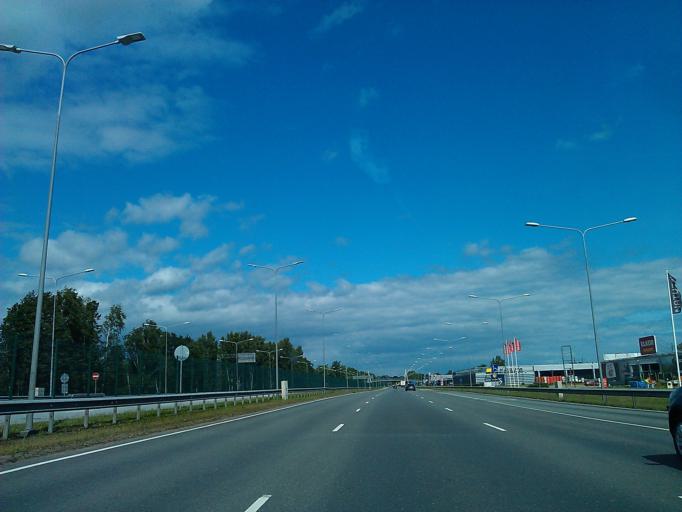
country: LV
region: Marupe
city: Marupe
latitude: 56.9343
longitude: 24.0051
